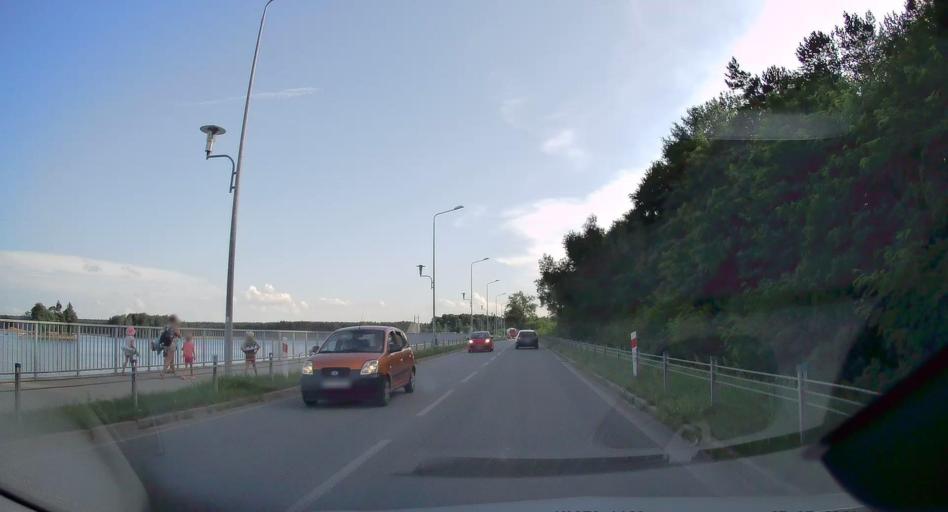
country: PL
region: Swietokrzyskie
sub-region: Powiat konecki
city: Smykow
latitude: 51.1165
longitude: 20.3507
